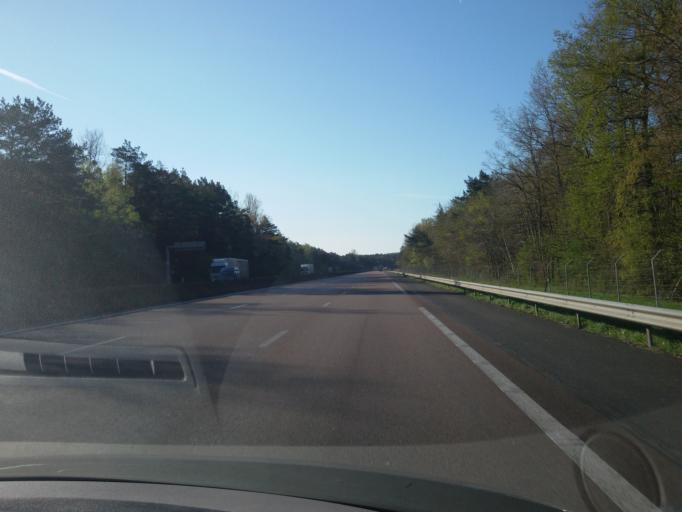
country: FR
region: Ile-de-France
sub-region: Departement de Seine-et-Marne
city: Arbonne-la-Foret
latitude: 48.4114
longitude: 2.5490
